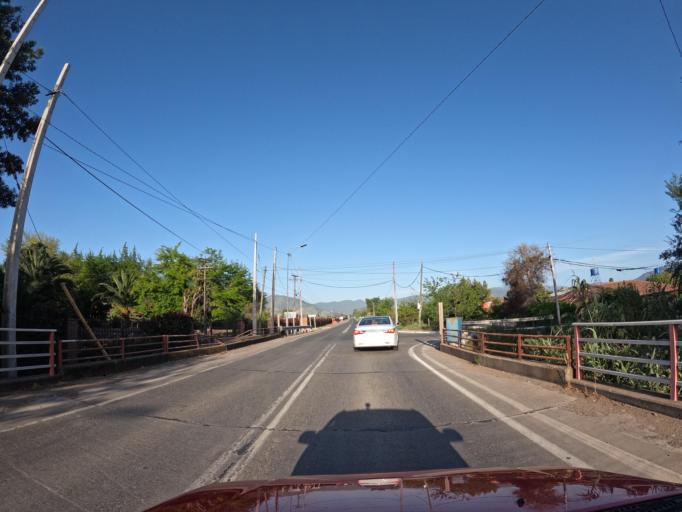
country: CL
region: O'Higgins
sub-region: Provincia de Colchagua
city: Santa Cruz
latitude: -34.5210
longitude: -71.3740
